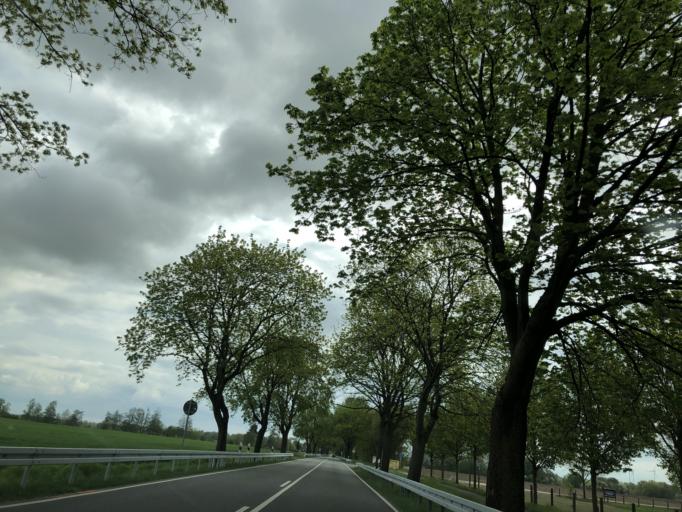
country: DE
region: Mecklenburg-Vorpommern
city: Lubz
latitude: 53.4655
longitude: 12.1184
